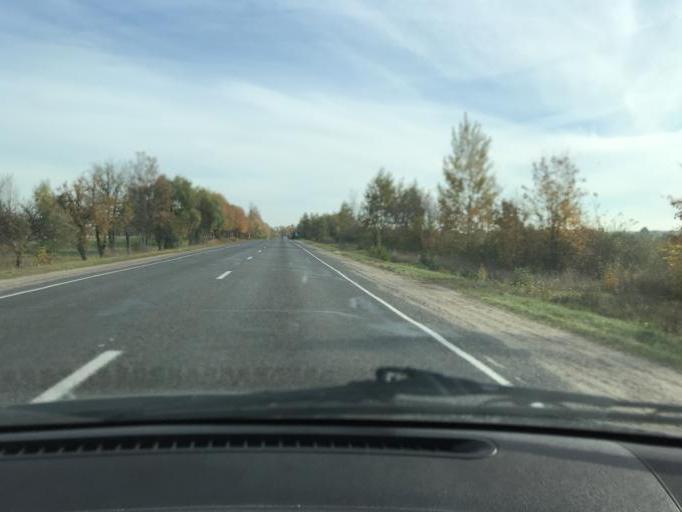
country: BY
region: Brest
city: Asnyezhytsy
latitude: 52.2026
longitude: 26.0599
